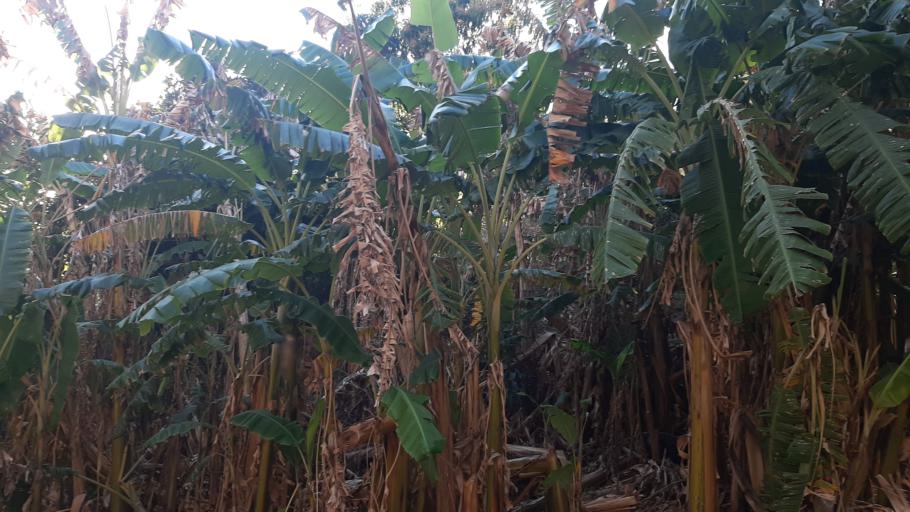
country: MX
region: Chihuahua
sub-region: Guadalupe y Calvo
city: Las Yerbitas [Aserradero]
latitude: 25.4305
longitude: -106.4717
